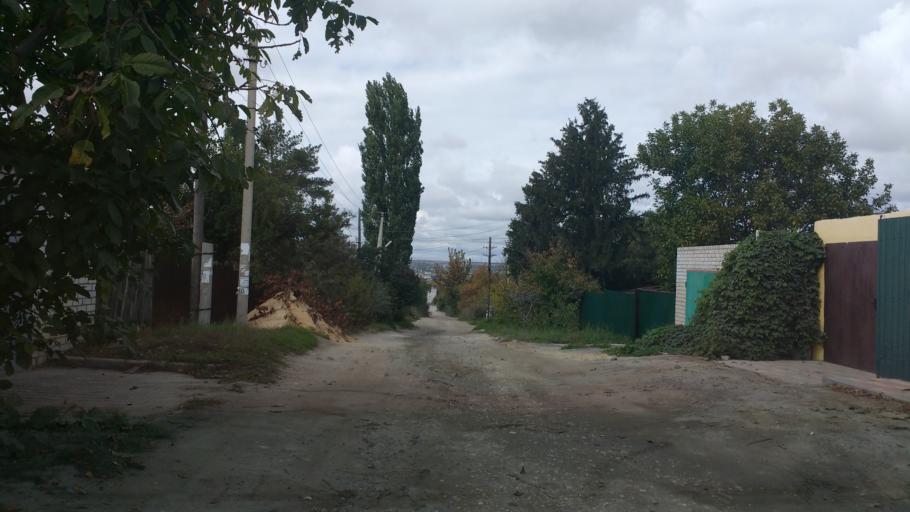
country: RU
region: Volgograd
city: Vodstroy
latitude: 48.7792
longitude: 44.5407
